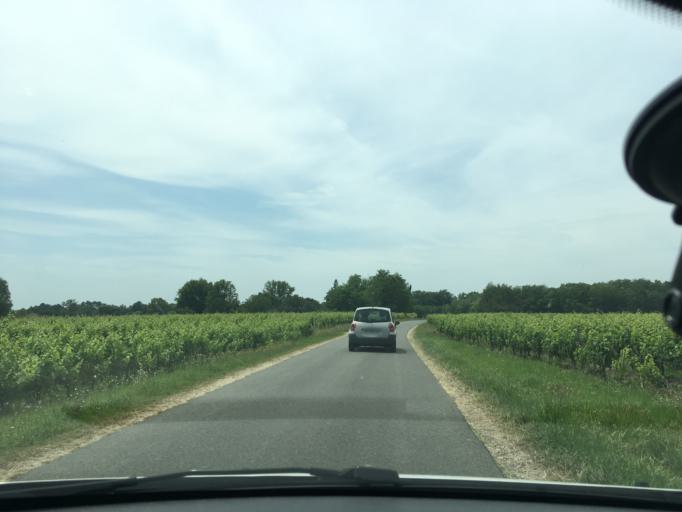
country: FR
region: Aquitaine
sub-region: Departement de la Gironde
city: Listrac-Medoc
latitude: 45.0547
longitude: -0.8075
